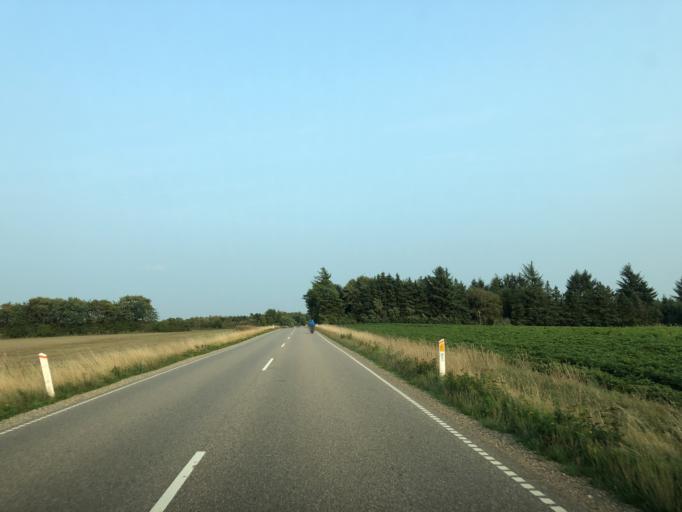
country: DK
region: South Denmark
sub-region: Billund Kommune
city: Grindsted
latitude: 55.8239
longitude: 8.9909
